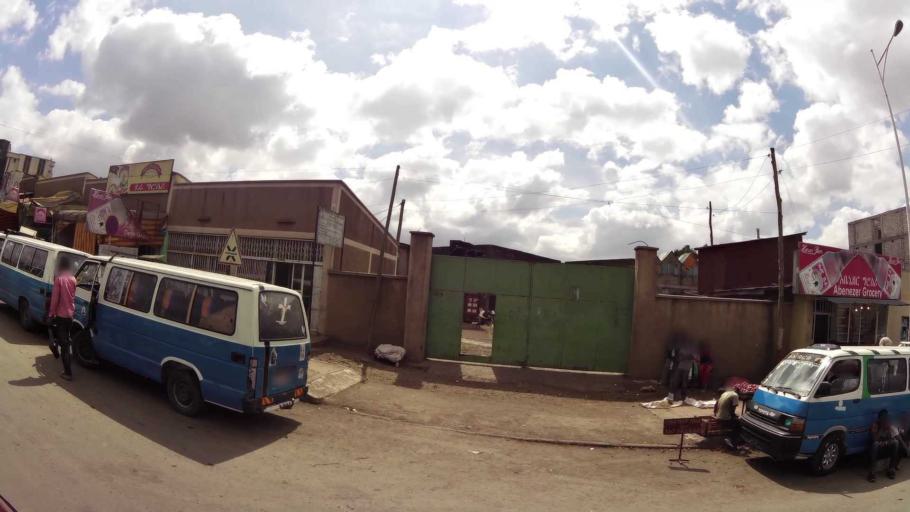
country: ET
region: Adis Abeba
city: Addis Ababa
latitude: 8.9527
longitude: 38.7619
